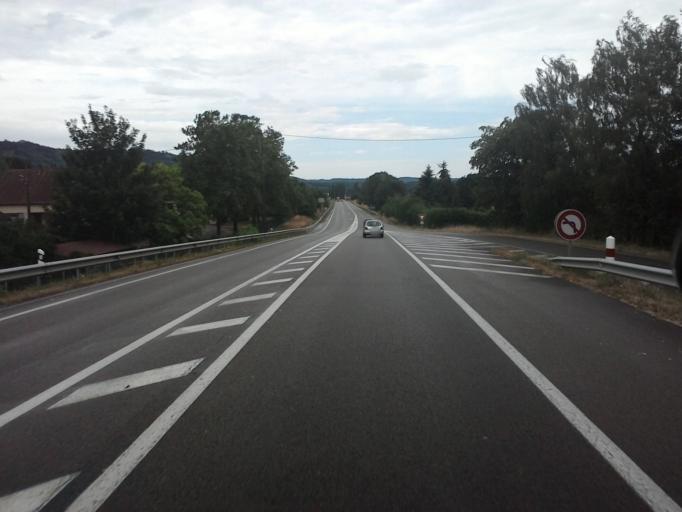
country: FR
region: Franche-Comte
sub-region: Departement du Jura
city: Poligny
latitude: 46.8442
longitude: 5.7019
